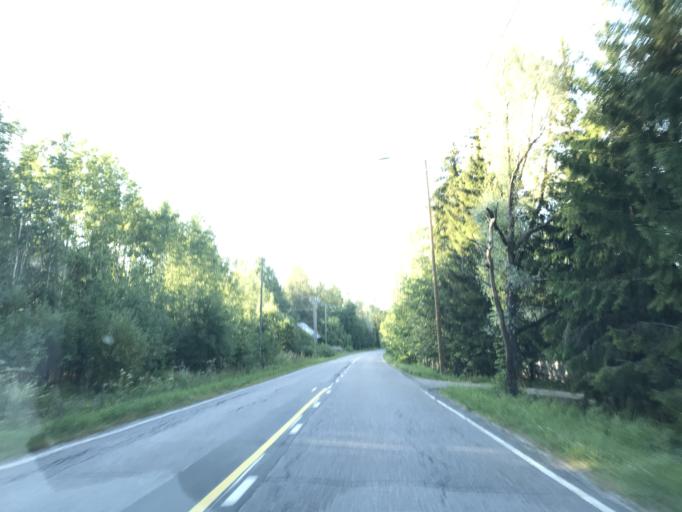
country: FI
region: Uusimaa
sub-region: Helsinki
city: Nurmijaervi
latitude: 60.3706
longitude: 24.6800
